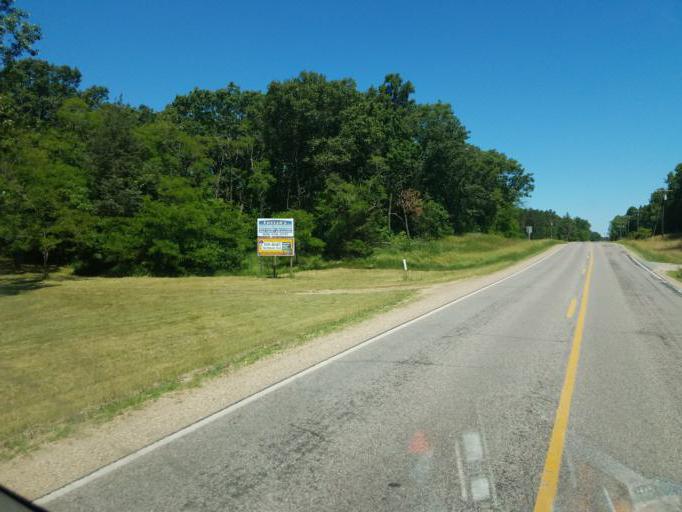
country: US
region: Wisconsin
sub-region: Adams County
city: Adams
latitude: 43.9279
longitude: -89.9374
